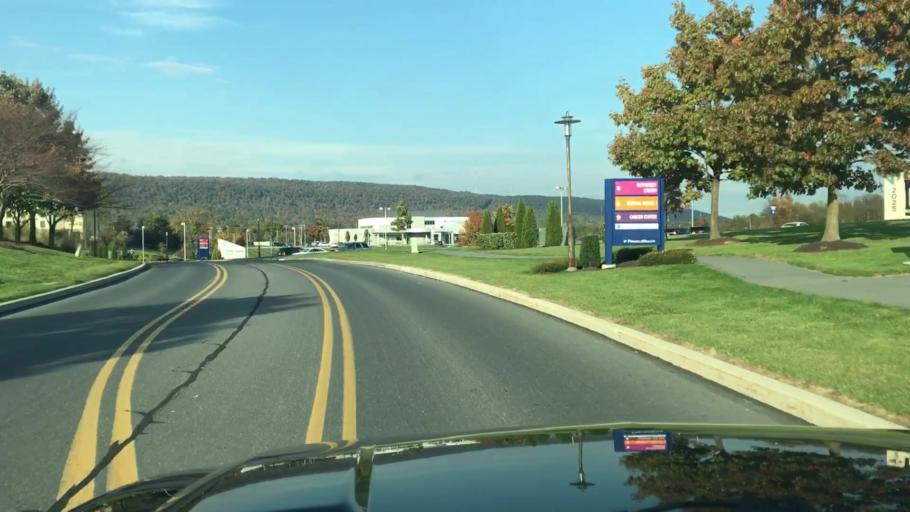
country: US
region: Pennsylvania
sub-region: Cumberland County
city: Enola
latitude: 40.2838
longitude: -76.9768
